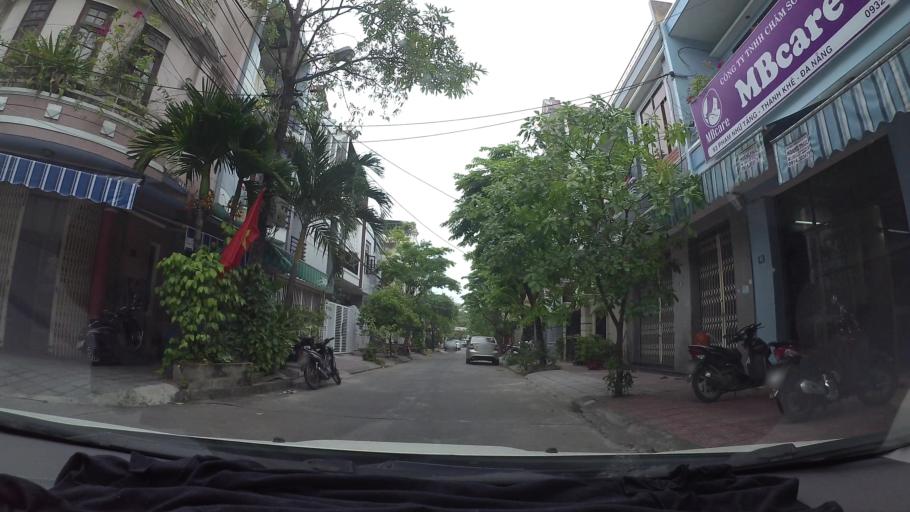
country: VN
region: Da Nang
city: Thanh Khe
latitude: 16.0636
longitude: 108.1924
